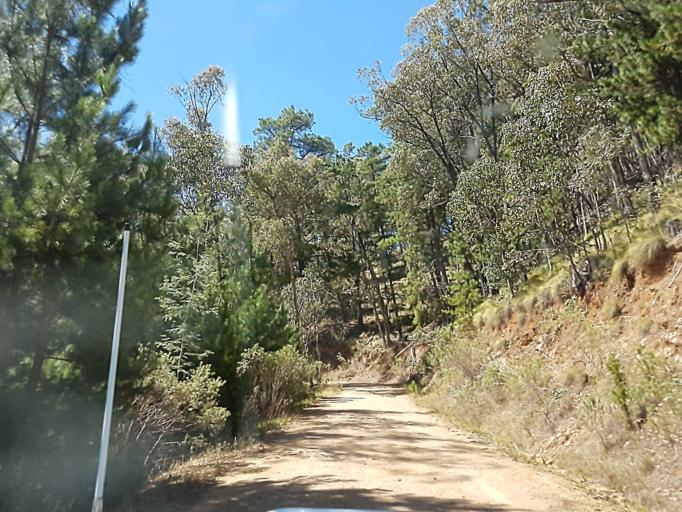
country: AU
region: Victoria
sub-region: Alpine
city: Mount Beauty
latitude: -36.7407
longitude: 146.9619
